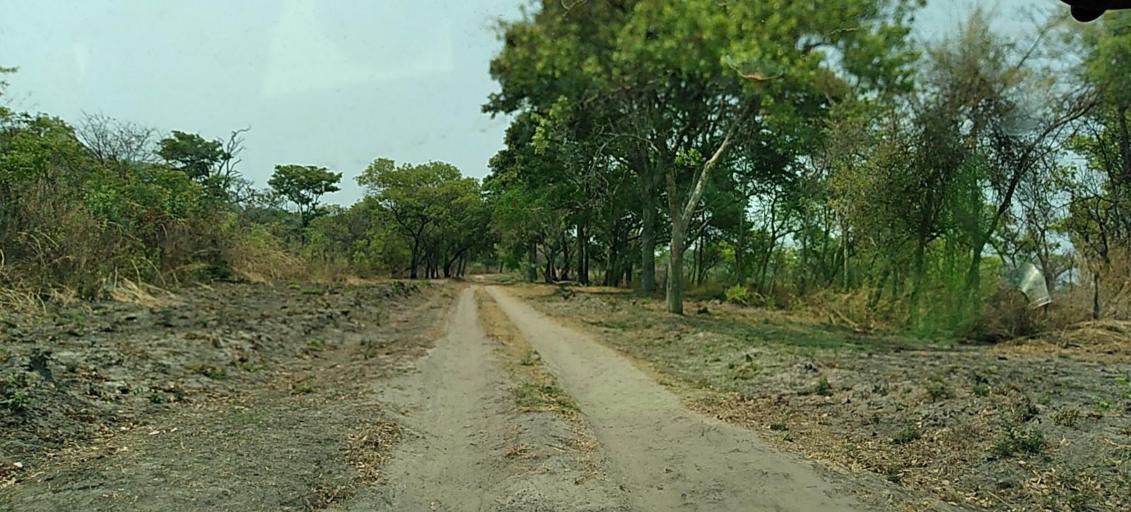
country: ZM
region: Western
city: Lukulu
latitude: -13.9670
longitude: 23.2279
